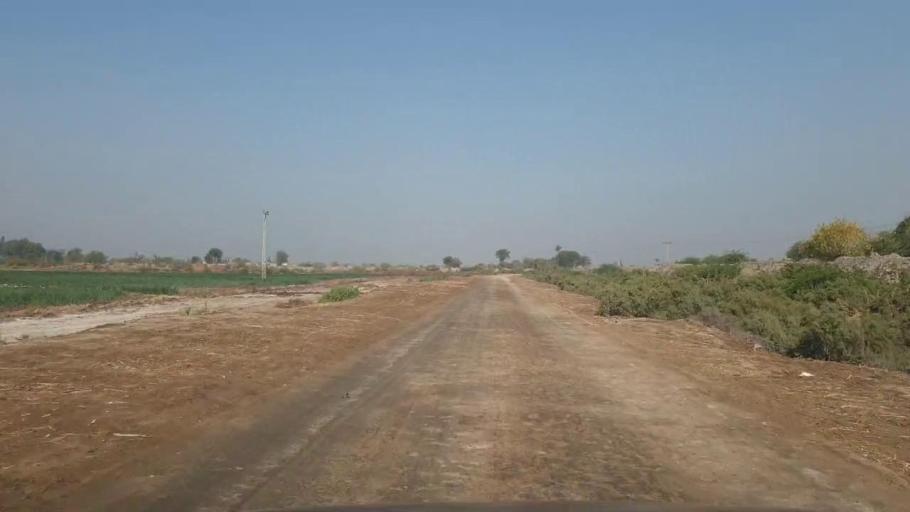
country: PK
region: Sindh
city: Mirwah Gorchani
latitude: 25.3724
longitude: 69.1874
